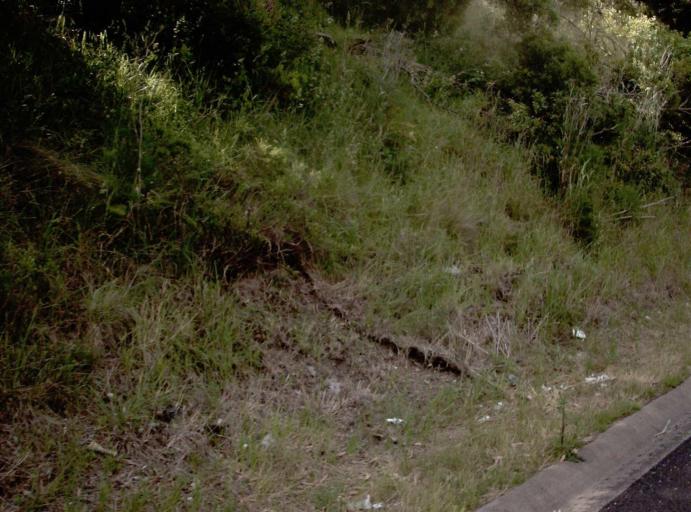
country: AU
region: Victoria
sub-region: East Gippsland
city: Lakes Entrance
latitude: -37.8504
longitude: 148.0381
